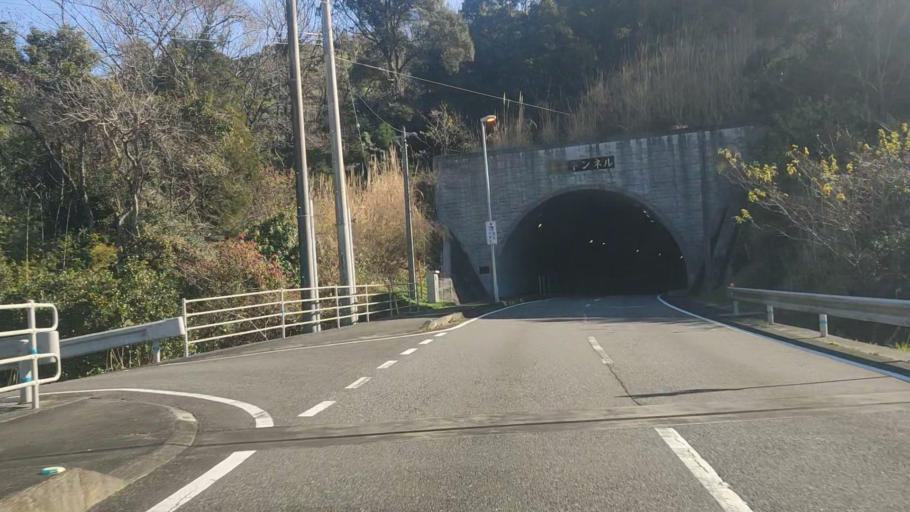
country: JP
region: Oita
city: Saiki
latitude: 32.8061
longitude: 131.8956
